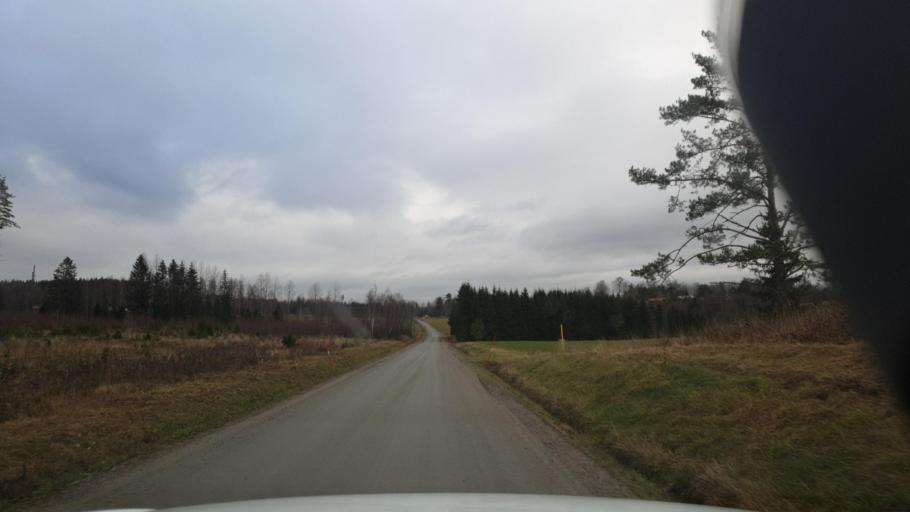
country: SE
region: Vaermland
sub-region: Karlstads Kommun
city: Edsvalla
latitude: 59.5486
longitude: 13.0091
